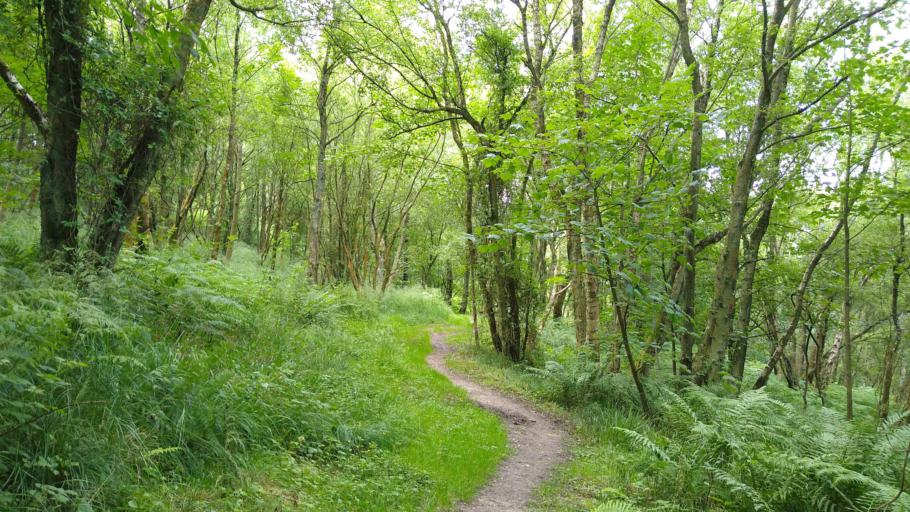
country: GB
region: England
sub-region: Northumberland
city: Greenhead
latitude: 54.9541
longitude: -2.4868
